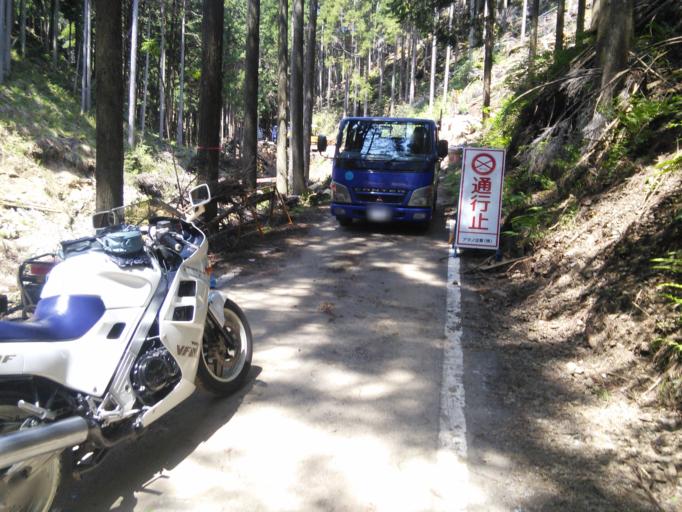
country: JP
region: Kyoto
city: Kameoka
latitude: 35.1595
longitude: 135.5727
